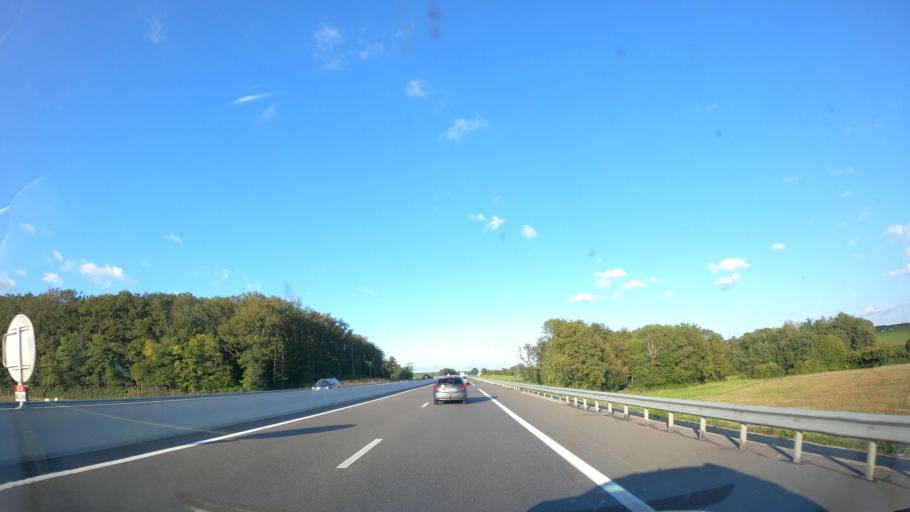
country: FR
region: Bourgogne
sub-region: Departement de Saone-et-Loire
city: Saint-Eusebe
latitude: 46.7161
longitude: 4.4370
